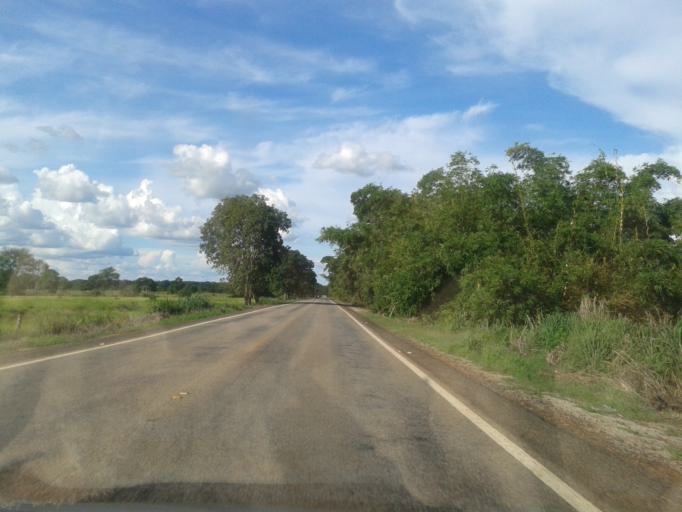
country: BR
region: Goias
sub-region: Mozarlandia
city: Mozarlandia
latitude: -14.5824
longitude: -50.5050
